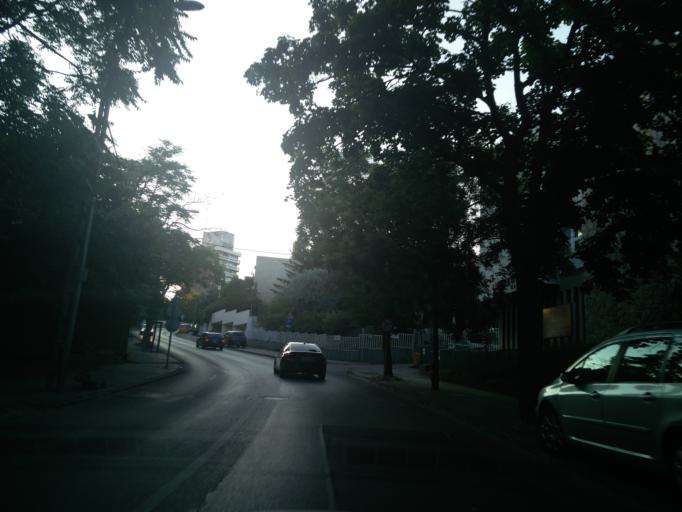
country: HU
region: Budapest
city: Budapest XII. keruelet
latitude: 47.5011
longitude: 19.0078
